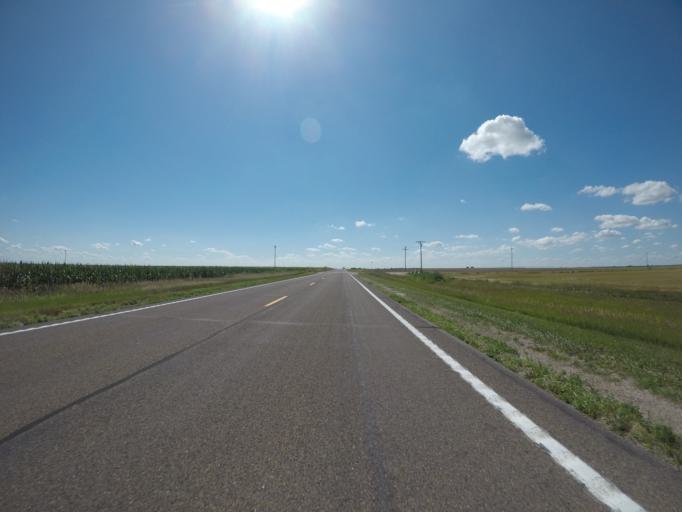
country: US
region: Nebraska
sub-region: Chase County
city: Imperial
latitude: 40.5378
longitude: -101.9107
